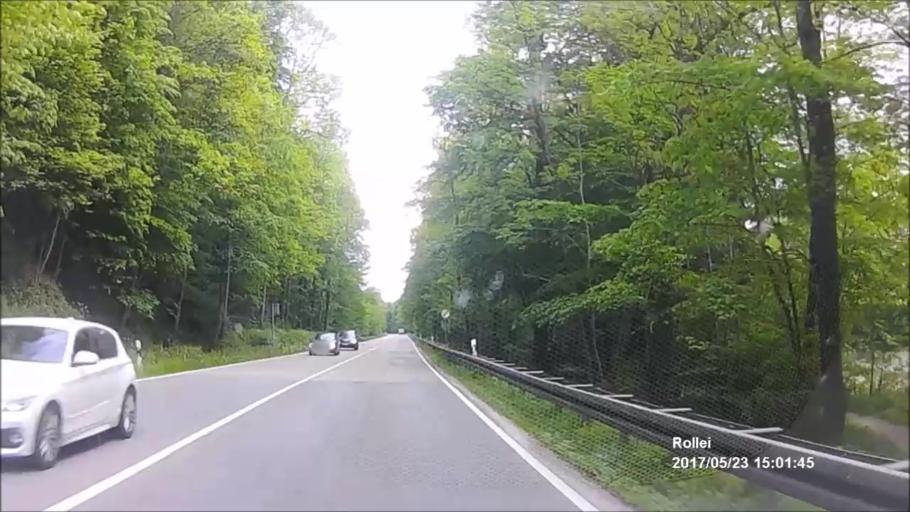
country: DE
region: Bavaria
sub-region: Upper Bavaria
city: Traunstein
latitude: 47.8553
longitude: 12.6387
